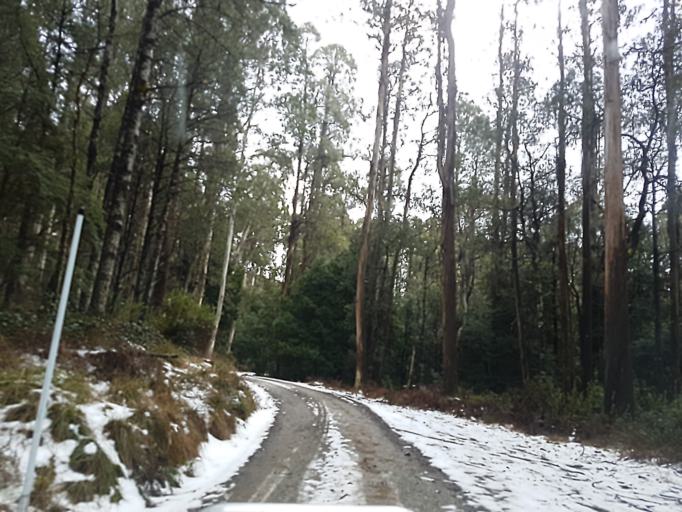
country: AU
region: Victoria
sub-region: Murrindindi
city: Alexandra
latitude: -37.4218
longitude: 145.8949
